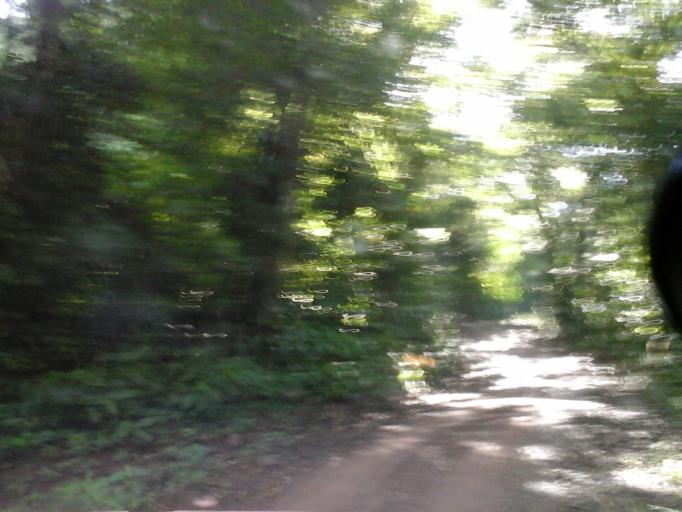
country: CO
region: Cesar
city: San Diego
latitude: 10.2629
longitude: -73.1070
